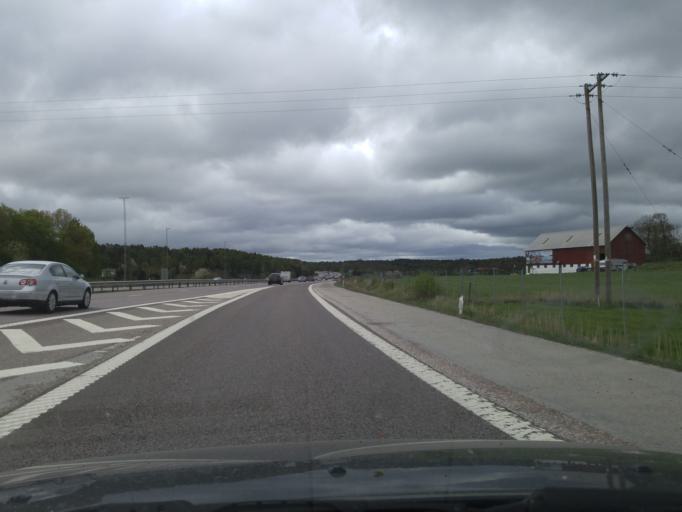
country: SE
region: Vaestra Goetaland
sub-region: Stenungsunds Kommun
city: Stora Hoga
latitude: 57.9822
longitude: 11.8412
